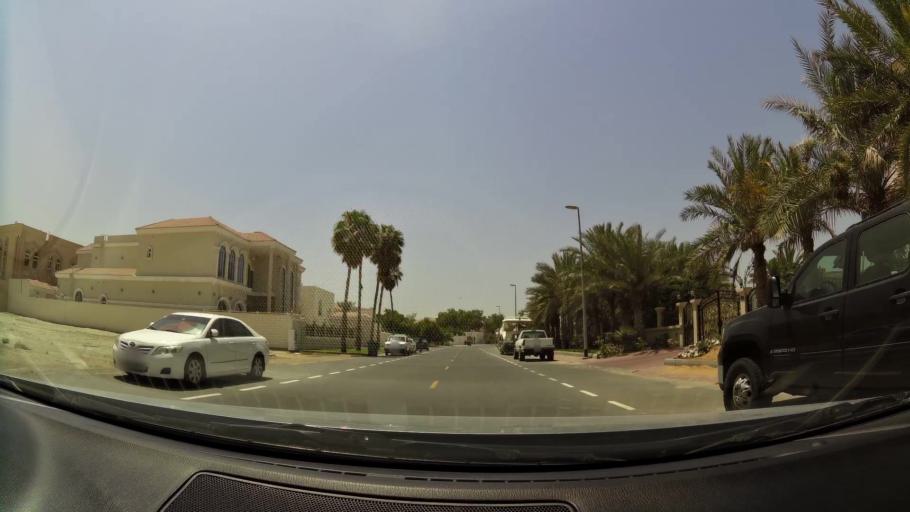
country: AE
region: Dubai
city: Dubai
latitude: 25.0949
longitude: 55.2054
